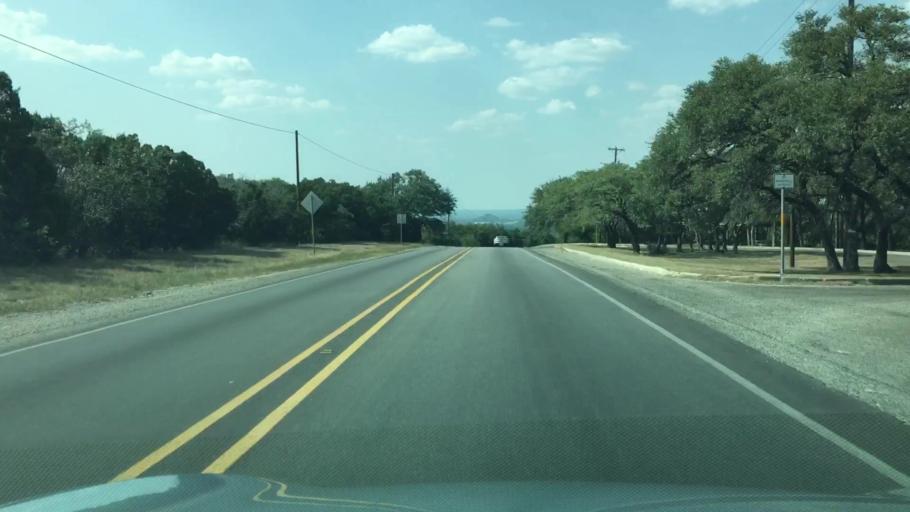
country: US
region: Texas
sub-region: Hays County
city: Wimberley
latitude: 29.9521
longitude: -98.0940
